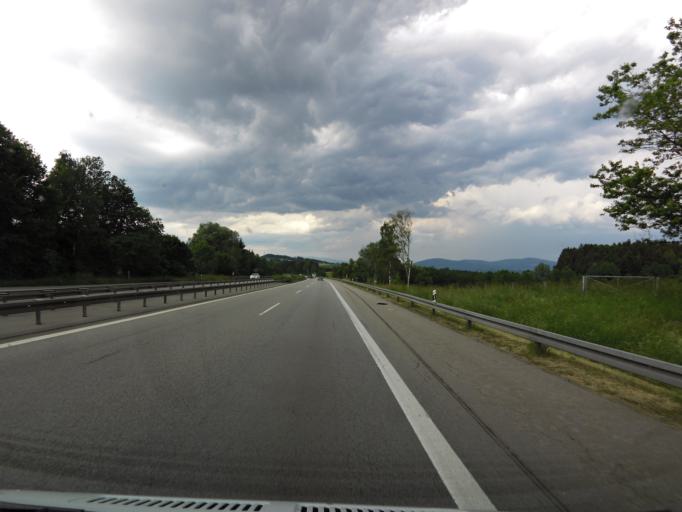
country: DE
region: Bavaria
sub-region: Lower Bavaria
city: Aussernzell
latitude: 48.6973
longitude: 13.1926
